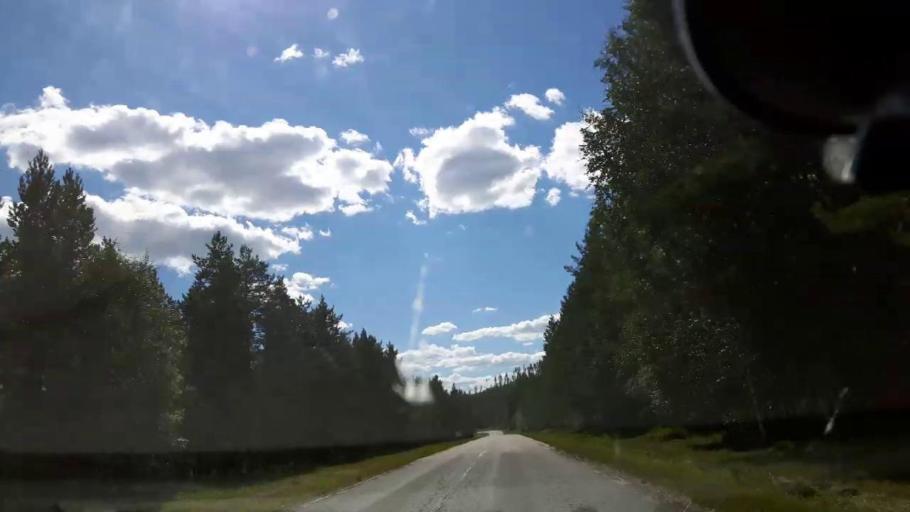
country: SE
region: Jaemtland
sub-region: Ragunda Kommun
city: Hammarstrand
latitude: 62.8713
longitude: 16.2203
